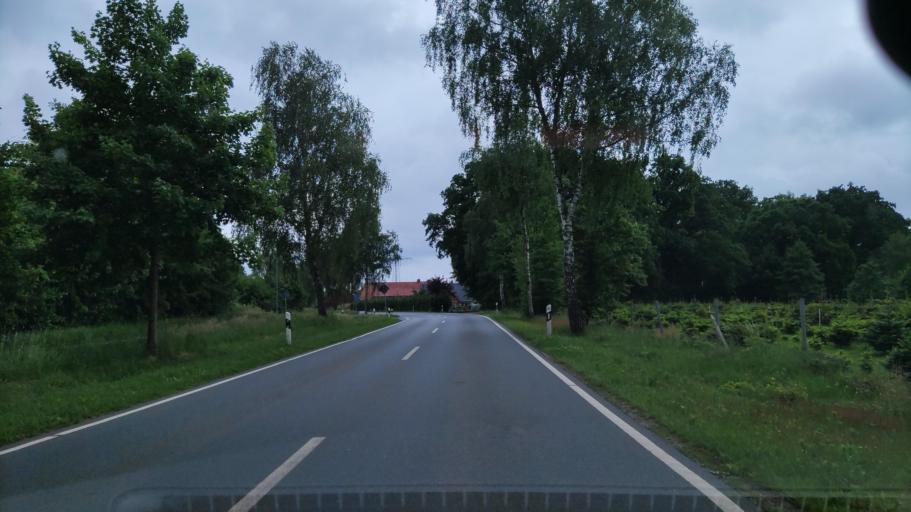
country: DE
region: Lower Saxony
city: Schneverdingen
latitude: 53.1147
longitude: 9.7658
